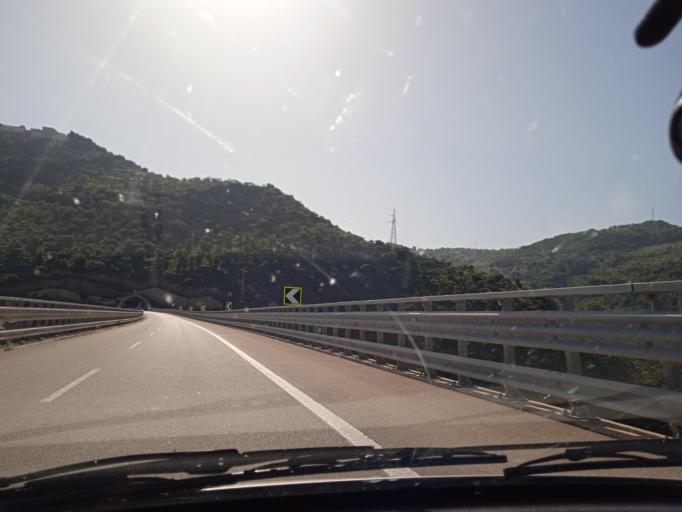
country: IT
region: Sicily
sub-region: Messina
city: Caronia
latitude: 38.0189
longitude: 14.4339
